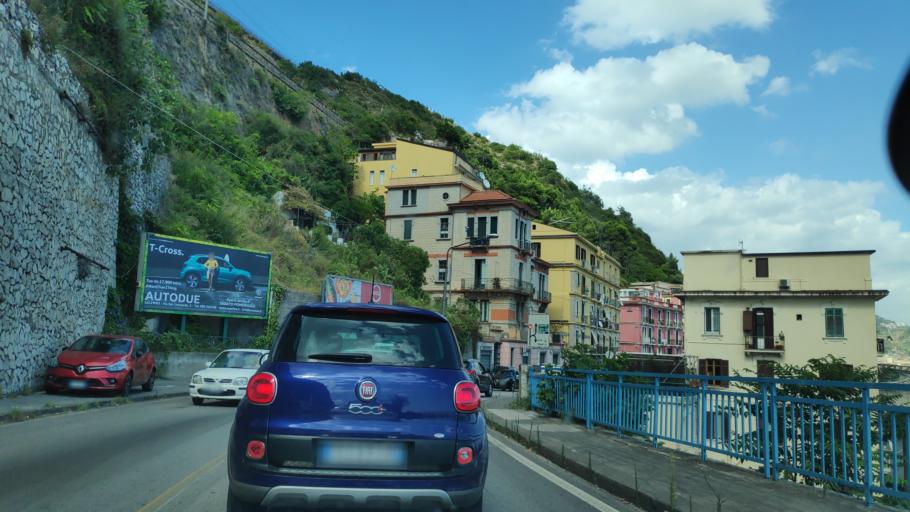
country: IT
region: Campania
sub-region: Provincia di Salerno
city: Vietri sul Mare
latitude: 40.6776
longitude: 14.7409
